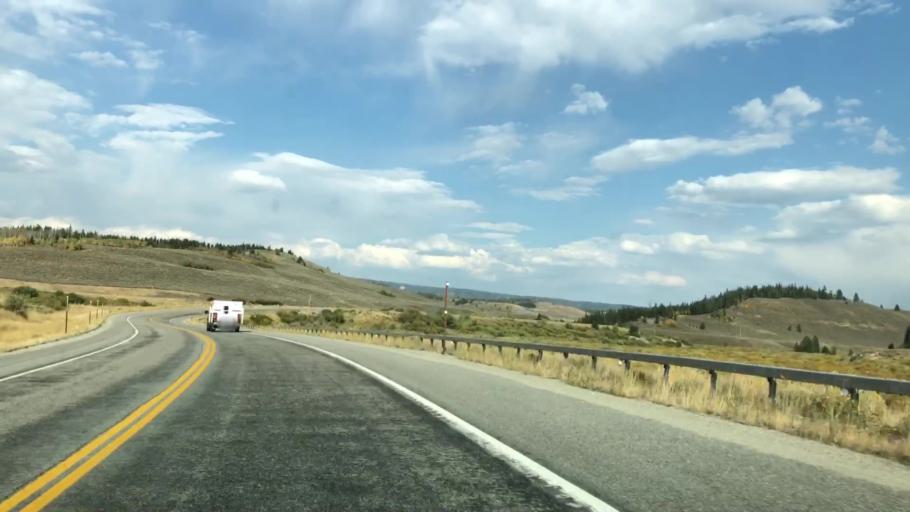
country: US
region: Wyoming
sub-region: Teton County
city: Hoback
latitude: 43.1531
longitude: -110.3356
